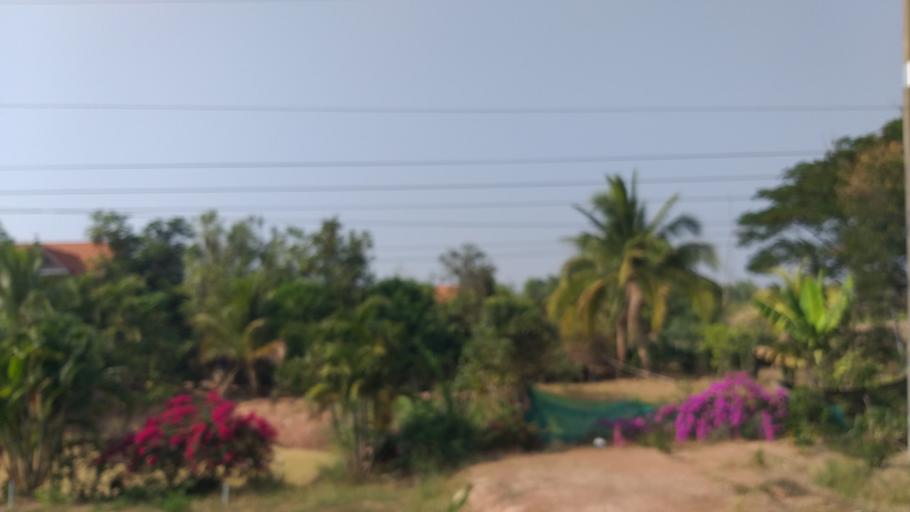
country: TH
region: Changwat Udon Thani
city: Thung Fon
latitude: 17.5249
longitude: 103.2133
